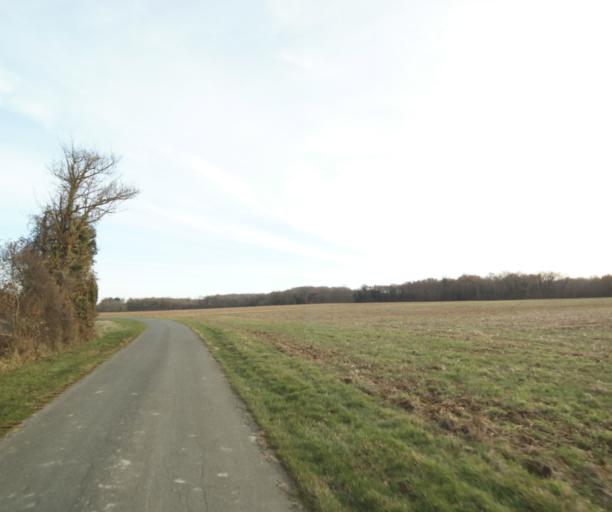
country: FR
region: Poitou-Charentes
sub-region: Departement de la Charente-Maritime
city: Saint-Hilaire-de-Villefranche
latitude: 45.8349
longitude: -0.5713
